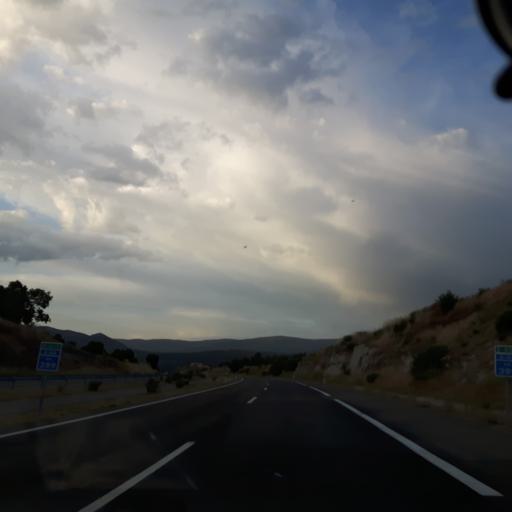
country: ES
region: Castille and Leon
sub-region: Provincia de Salamanca
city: Nava de Bejar
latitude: 40.4720
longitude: -5.6821
